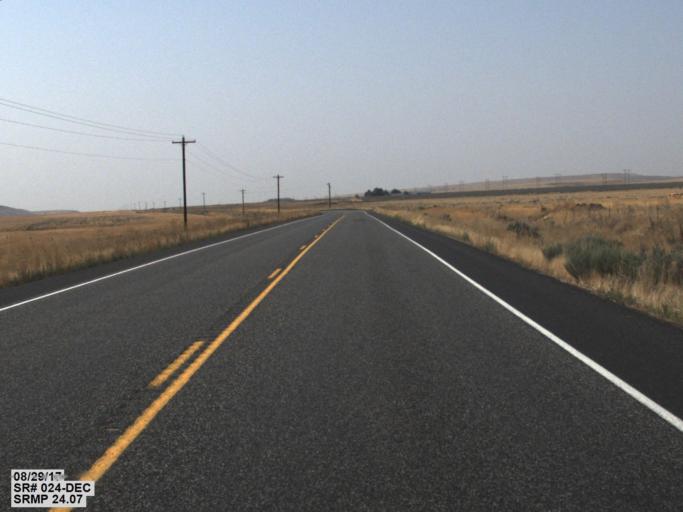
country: US
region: Washington
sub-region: Grant County
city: Desert Aire
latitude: 46.5198
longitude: -120.0090
